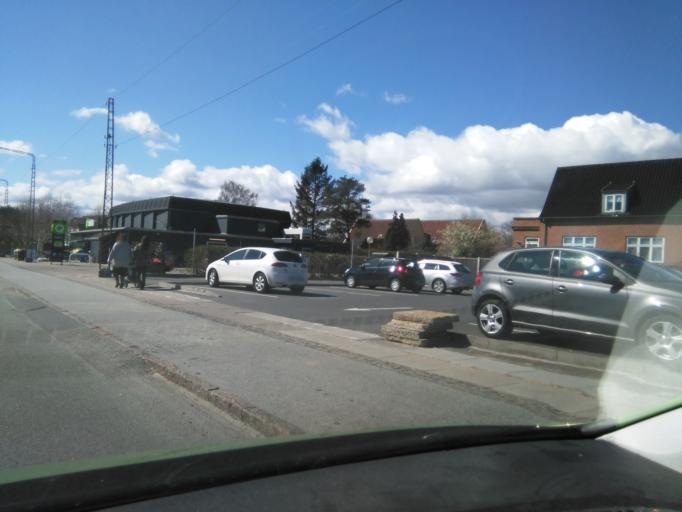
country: DK
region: Central Jutland
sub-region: Arhus Kommune
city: Lystrup
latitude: 56.1929
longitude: 10.2431
